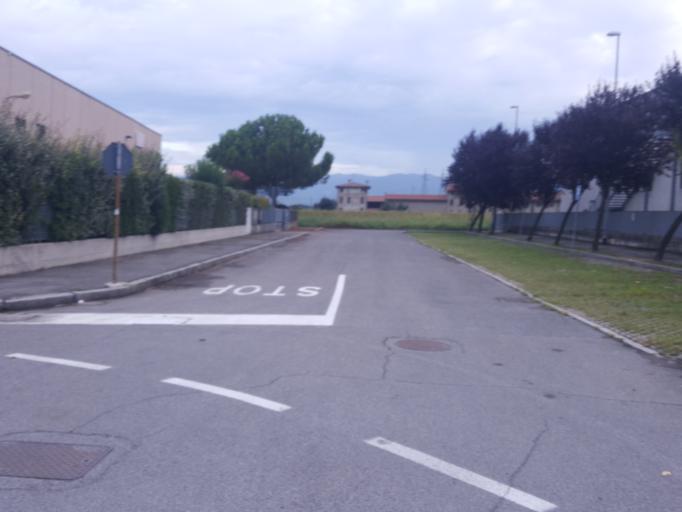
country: IT
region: Lombardy
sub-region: Provincia di Brescia
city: Torbole Casaglia
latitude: 45.5191
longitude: 10.1323
